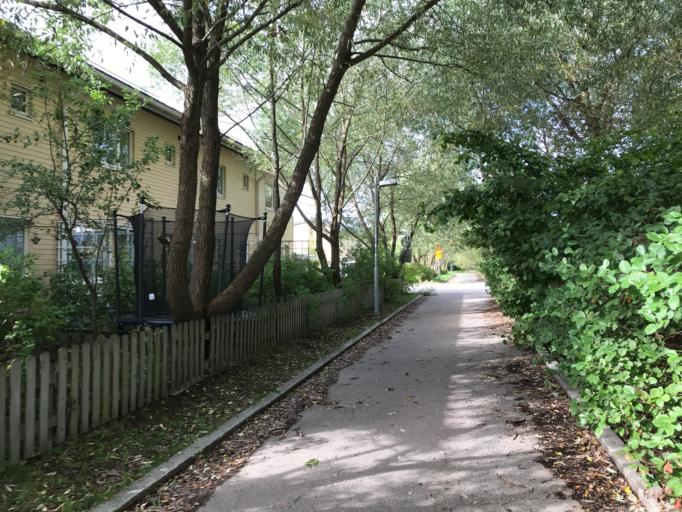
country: FI
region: Uusimaa
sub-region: Helsinki
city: Vantaa
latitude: 60.2255
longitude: 25.0286
